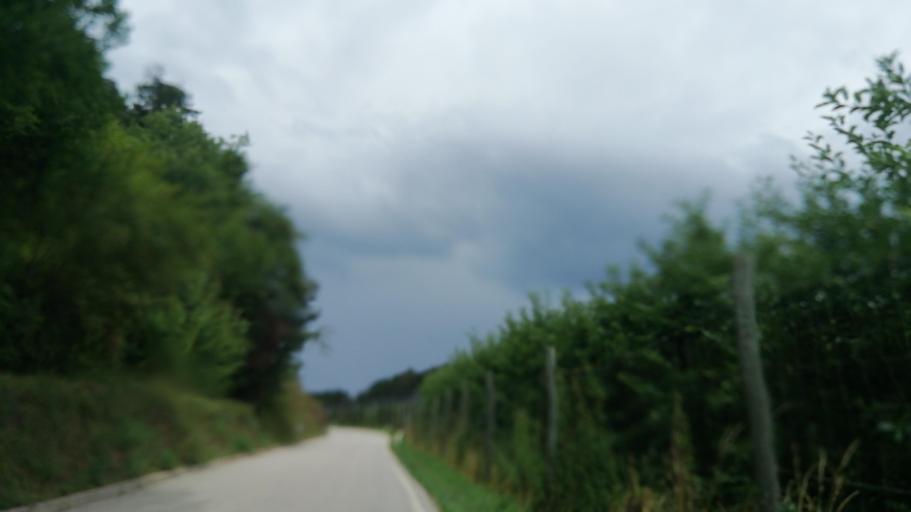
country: IT
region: Trentino-Alto Adige
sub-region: Provincia di Trento
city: Verla
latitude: 46.1703
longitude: 11.1634
